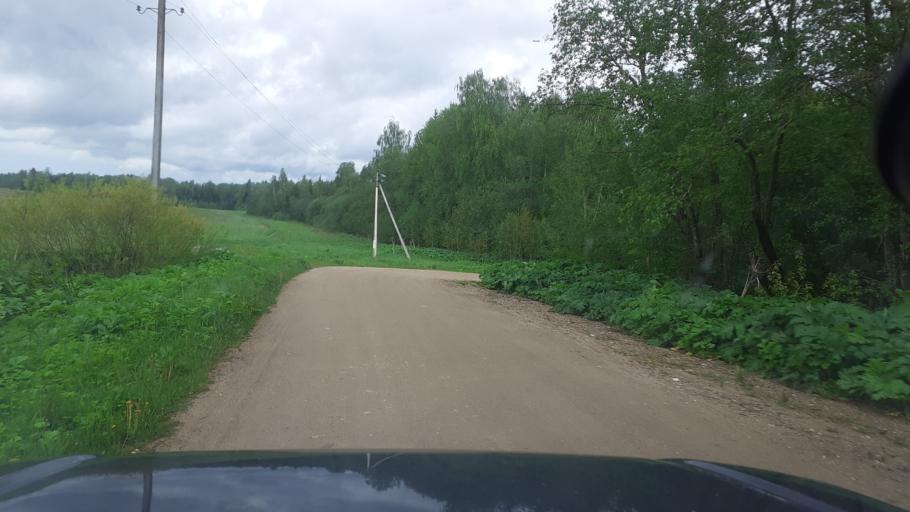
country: RU
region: Moskovskaya
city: Sychevo
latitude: 55.9643
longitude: 36.2514
